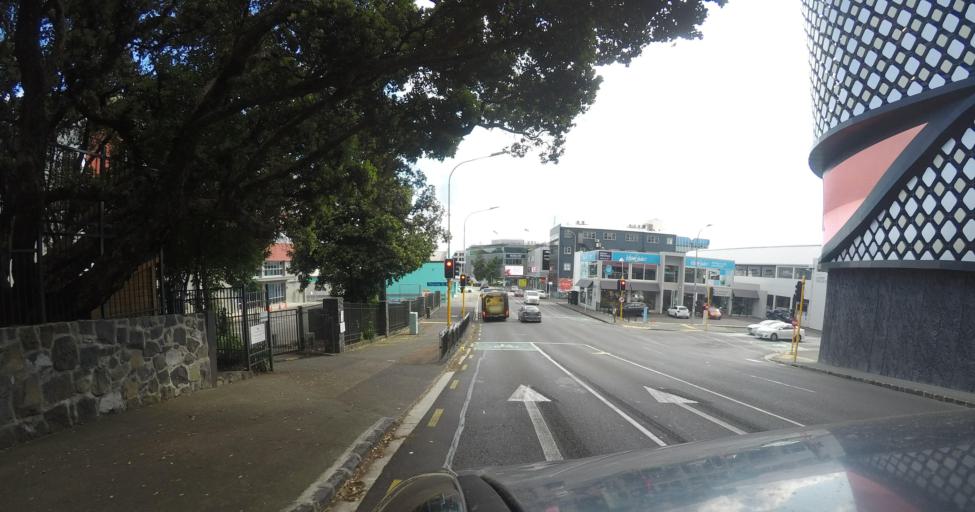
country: NZ
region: Auckland
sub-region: Auckland
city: Auckland
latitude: -36.8702
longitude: 174.7747
